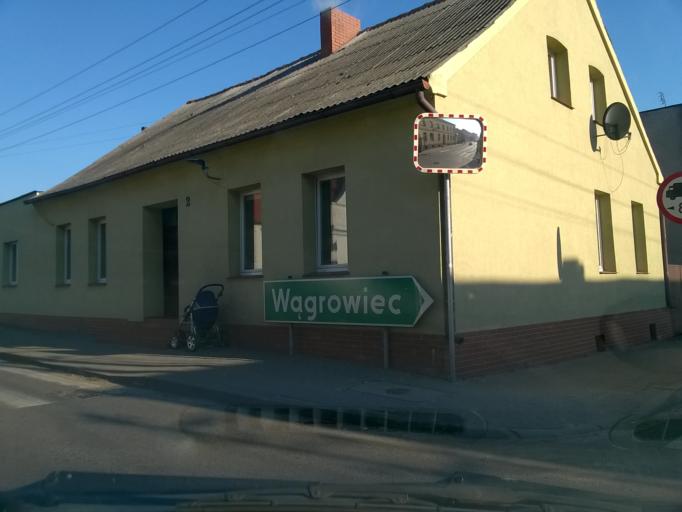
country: PL
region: Greater Poland Voivodeship
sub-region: Powiat wagrowiecki
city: Golancz
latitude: 52.9448
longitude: 17.3021
